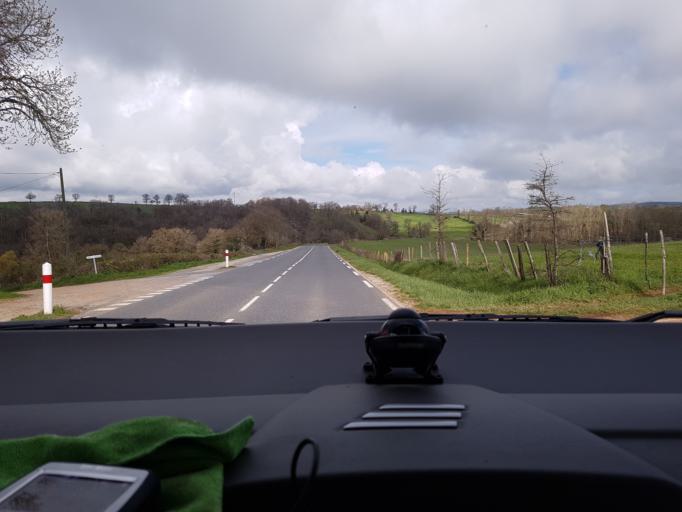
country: FR
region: Midi-Pyrenees
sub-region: Departement de l'Aveyron
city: Moyrazes
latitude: 44.3723
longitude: 2.4620
